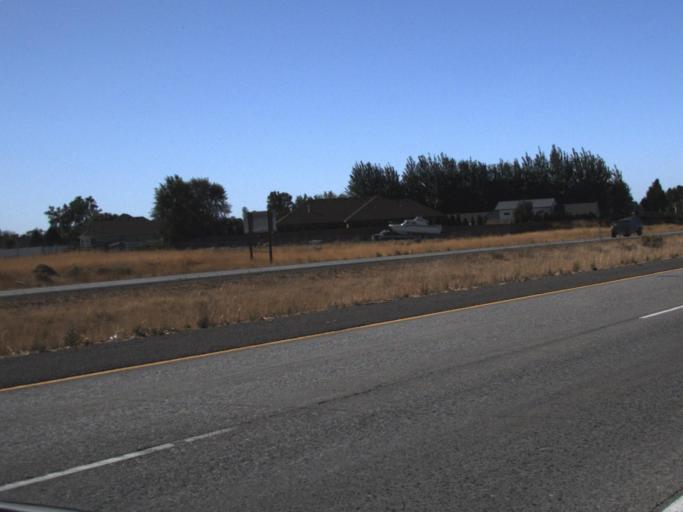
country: US
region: Washington
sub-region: Franklin County
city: West Pasco
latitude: 46.2540
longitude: -119.1440
